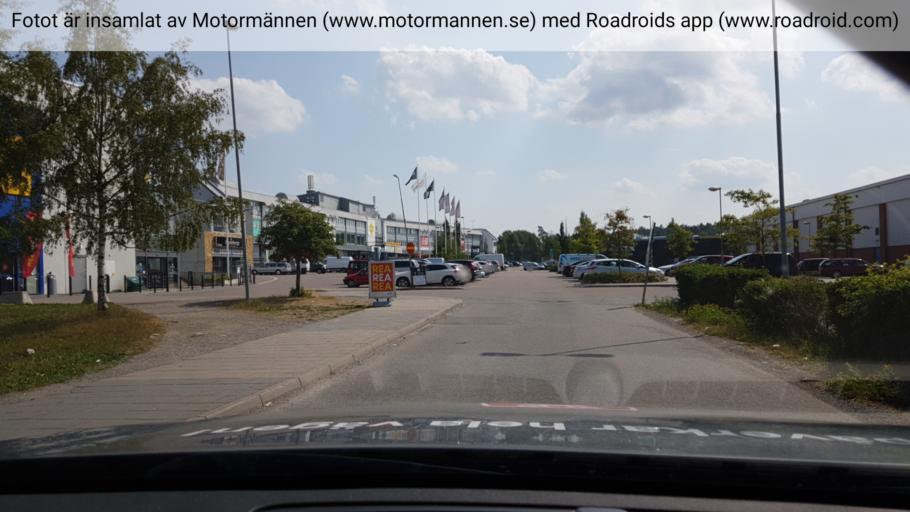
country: SE
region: Stockholm
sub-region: Huddinge Kommun
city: Segeltorp
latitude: 59.2694
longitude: 17.9221
